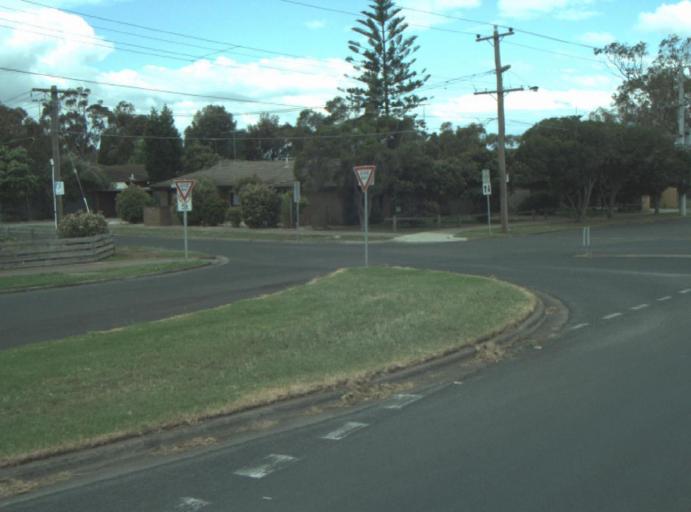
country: AU
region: Victoria
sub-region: Greater Geelong
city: Bell Park
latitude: -38.0714
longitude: 144.3588
